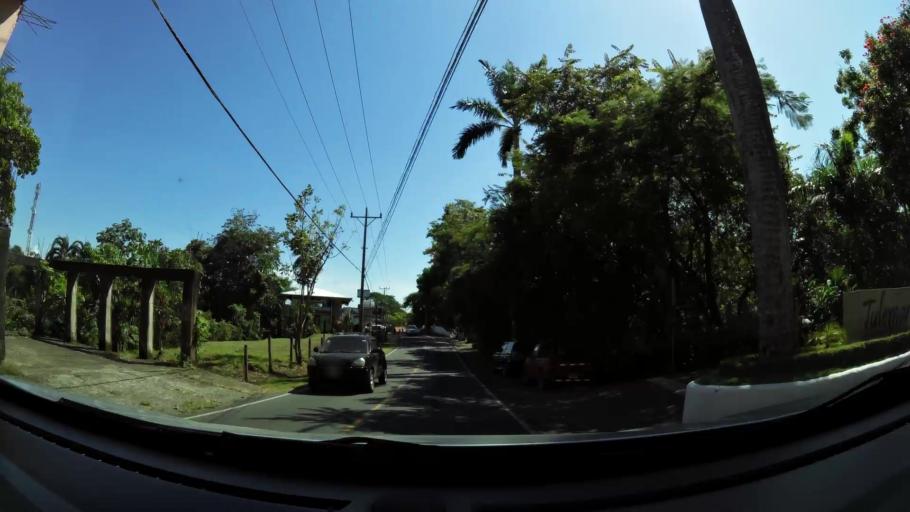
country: CR
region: Puntarenas
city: Quepos
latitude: 9.4077
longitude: -84.1582
